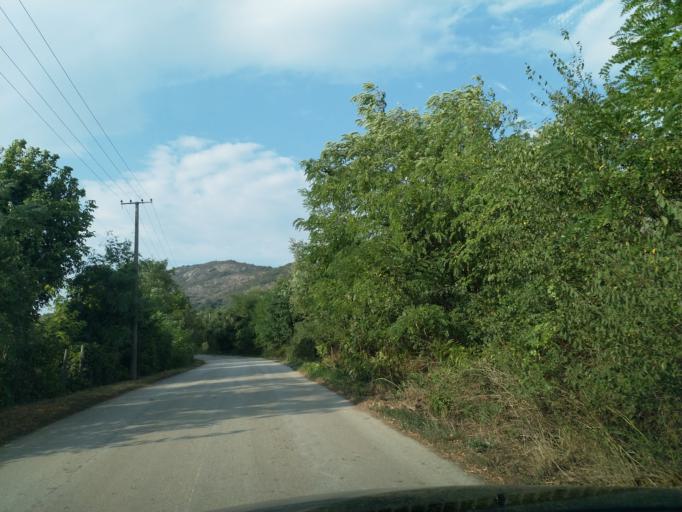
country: RS
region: Central Serbia
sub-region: Pomoravski Okrug
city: Paracin
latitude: 43.8301
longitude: 21.5420
